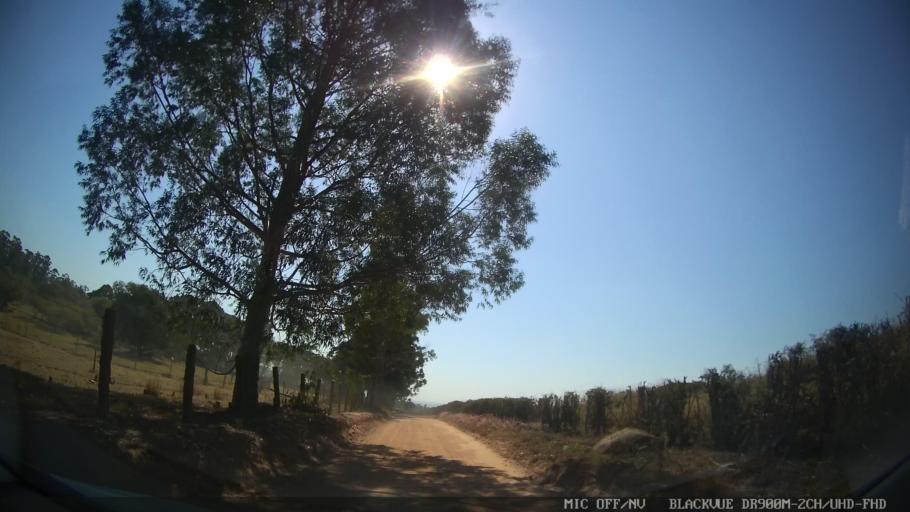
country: BR
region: Sao Paulo
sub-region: Itupeva
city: Itupeva
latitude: -23.0810
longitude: -47.0910
